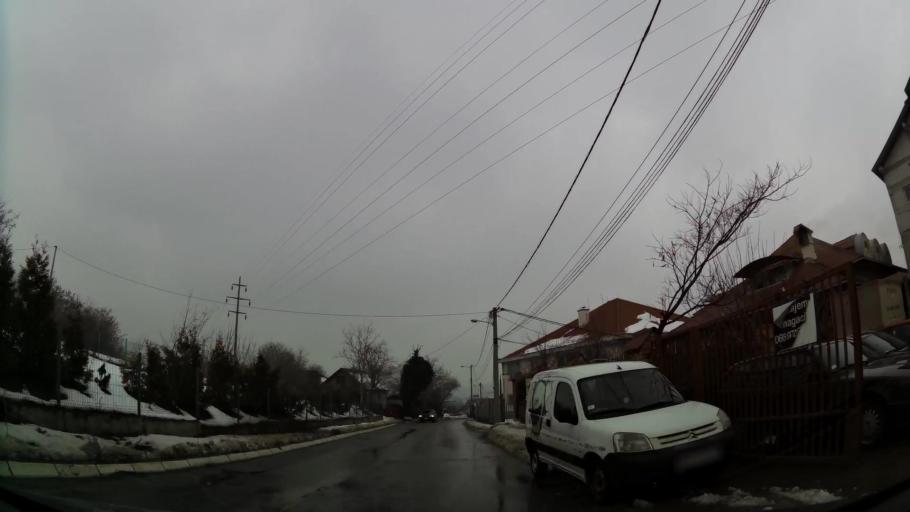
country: RS
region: Central Serbia
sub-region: Belgrade
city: Zvezdara
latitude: 44.7678
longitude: 20.5178
